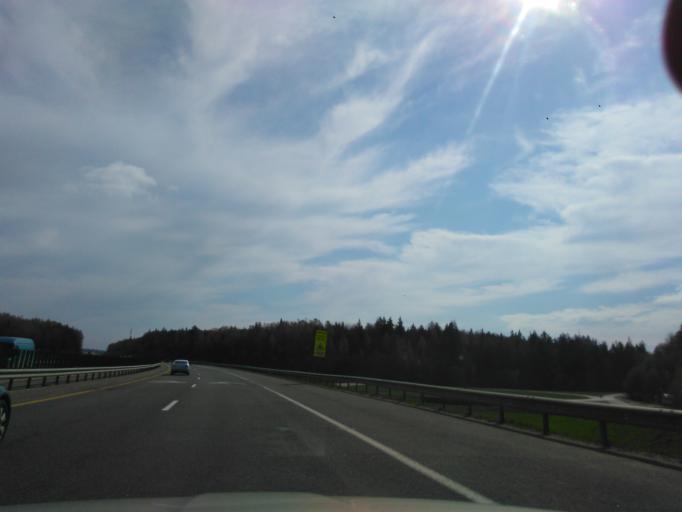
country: BY
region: Minsk
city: Novosel'ye
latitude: 53.9121
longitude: 27.2534
